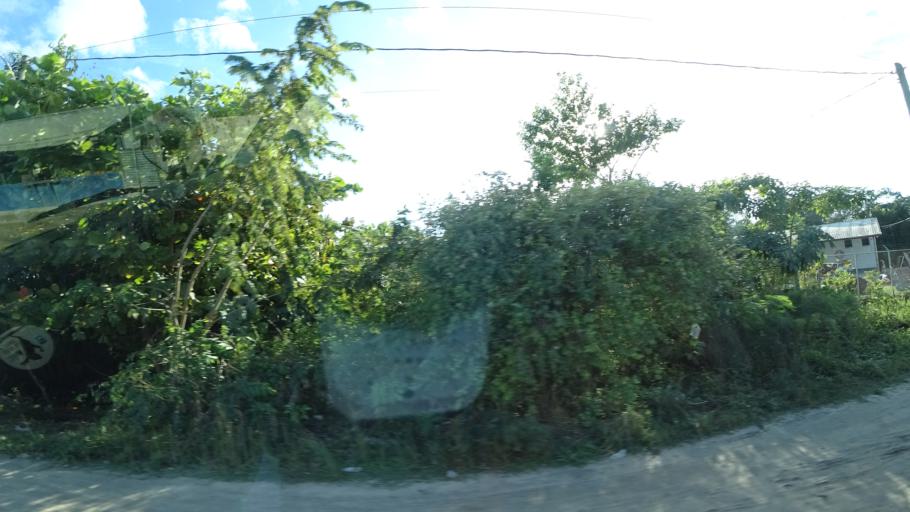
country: BZ
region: Belize
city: Belize City
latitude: 17.5499
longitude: -88.3027
